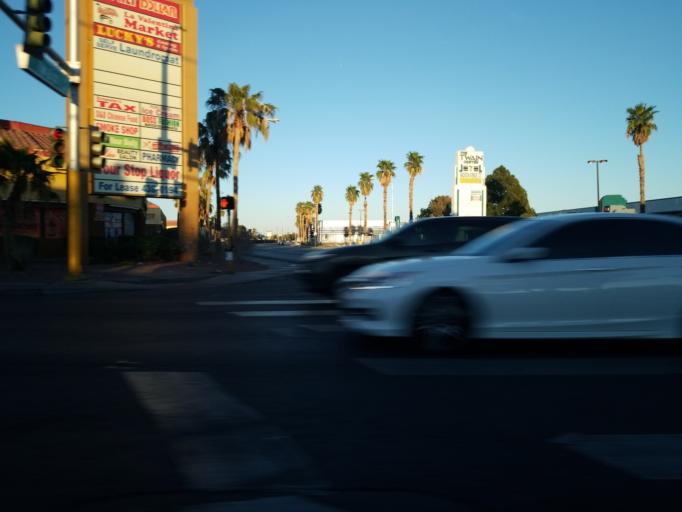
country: US
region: Nevada
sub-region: Clark County
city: Paradise
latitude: 36.1219
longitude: -115.1461
